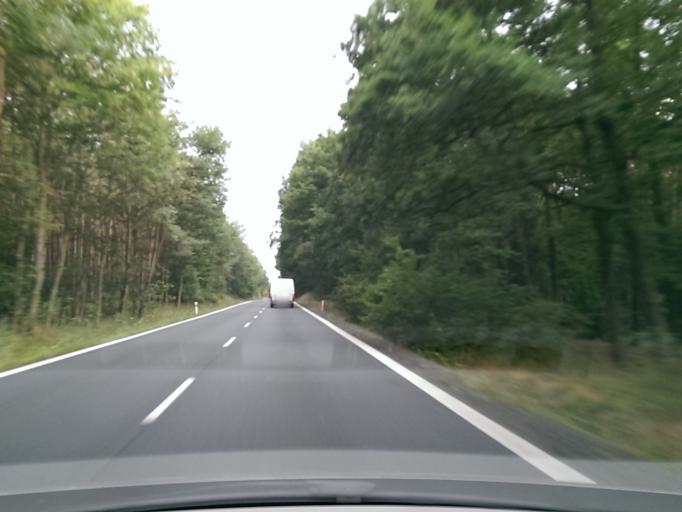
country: CZ
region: Central Bohemia
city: Loucen
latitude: 50.2617
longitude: 14.9784
